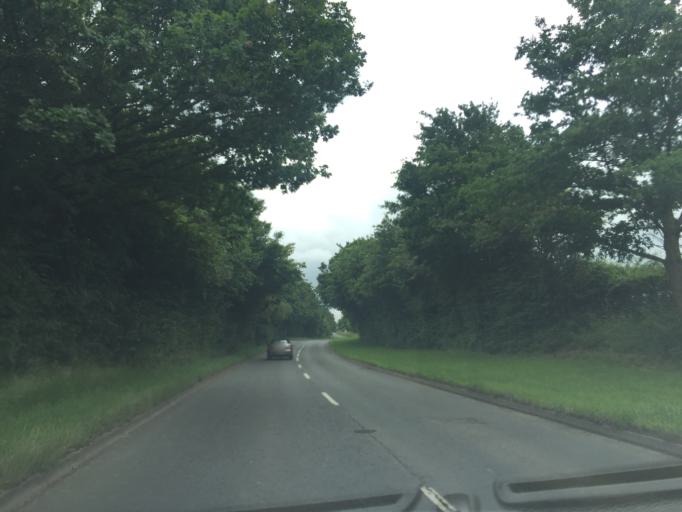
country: GB
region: England
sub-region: Greater London
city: Collier Row
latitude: 51.6513
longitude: 0.1704
